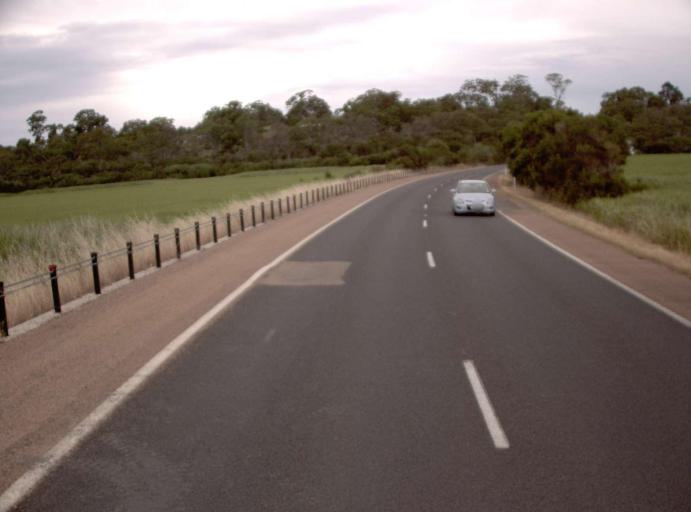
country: AU
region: Victoria
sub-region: East Gippsland
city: Bairnsdale
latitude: -37.8862
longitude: 147.6598
